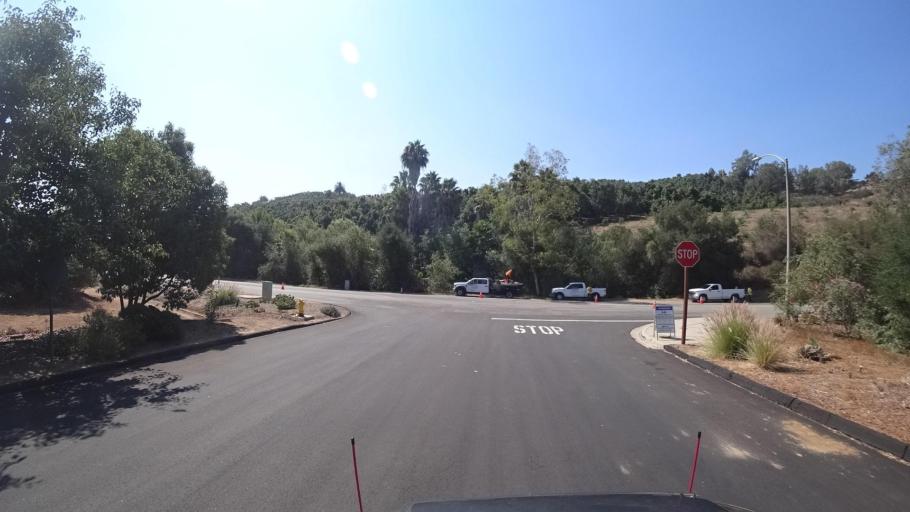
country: US
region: California
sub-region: San Diego County
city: Bonsall
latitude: 33.2534
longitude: -117.1904
